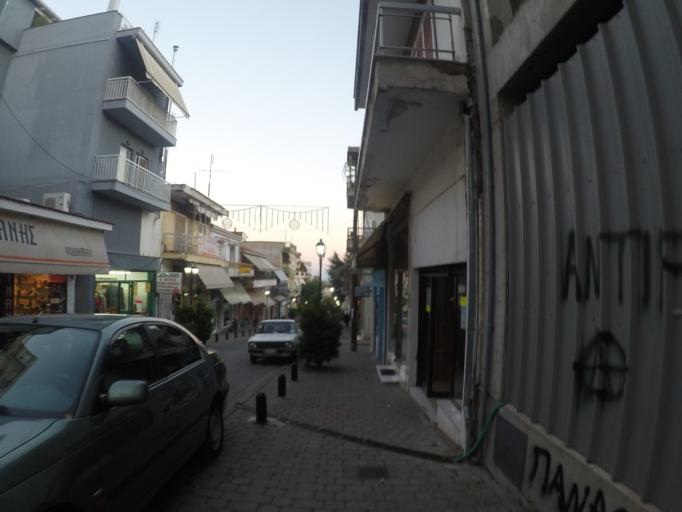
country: GR
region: Thessaly
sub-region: Trikala
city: Kalampaka
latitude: 39.7075
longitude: 21.6248
